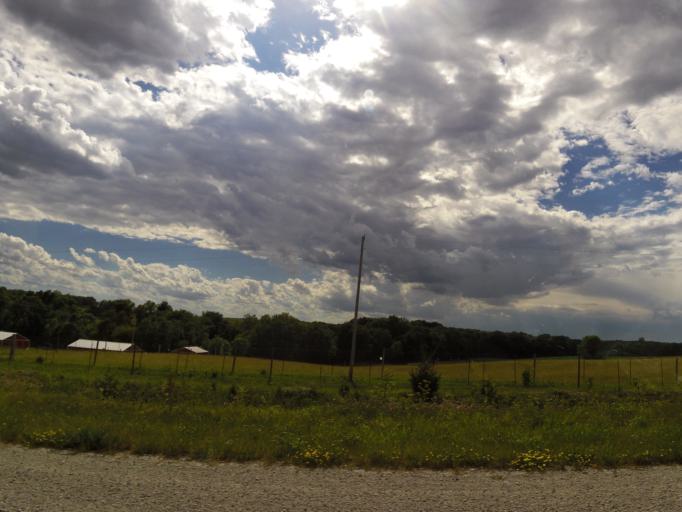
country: US
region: Iowa
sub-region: Henry County
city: Mount Pleasant
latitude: 40.8652
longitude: -91.5653
